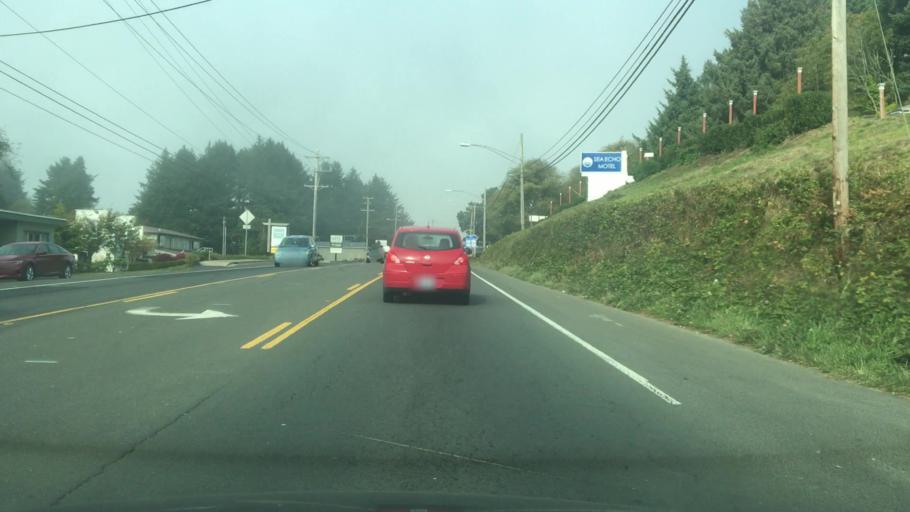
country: US
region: Oregon
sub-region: Lincoln County
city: Lincoln City
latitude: 44.9910
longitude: -124.0061
